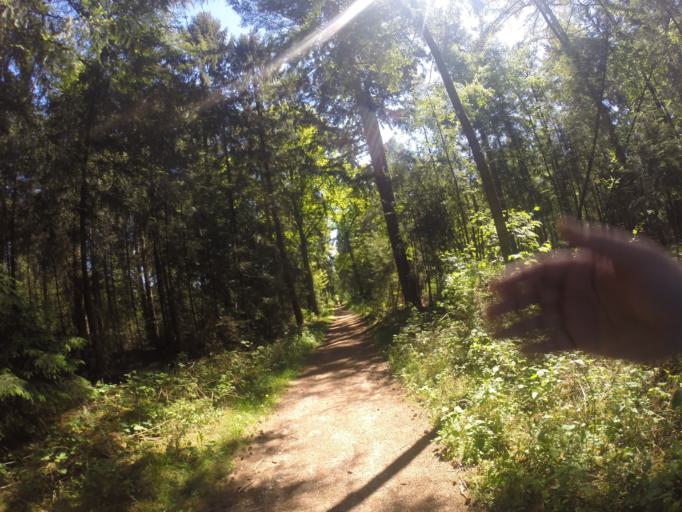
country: NL
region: Gelderland
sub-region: Gemeente Montferland
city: s-Heerenberg
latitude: 51.8882
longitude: 6.2085
